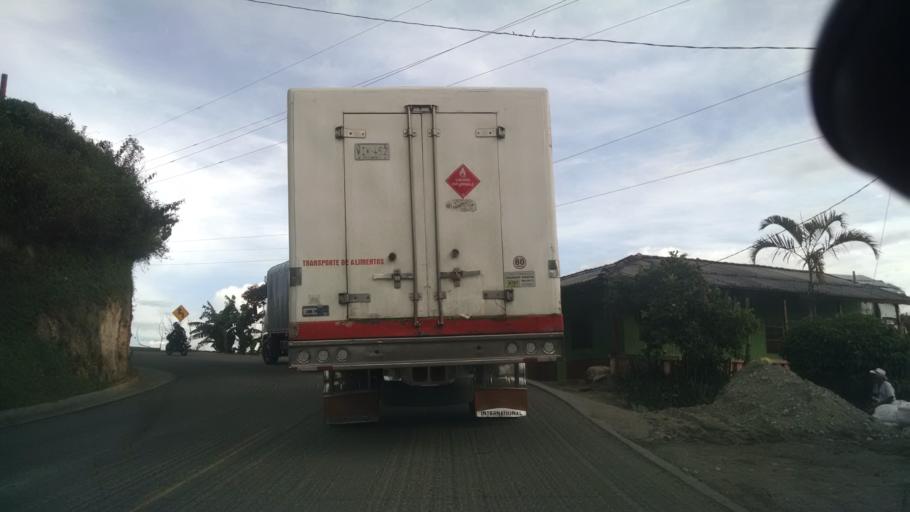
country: CO
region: Antioquia
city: Santa Barbara
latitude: 5.9010
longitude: -75.5751
